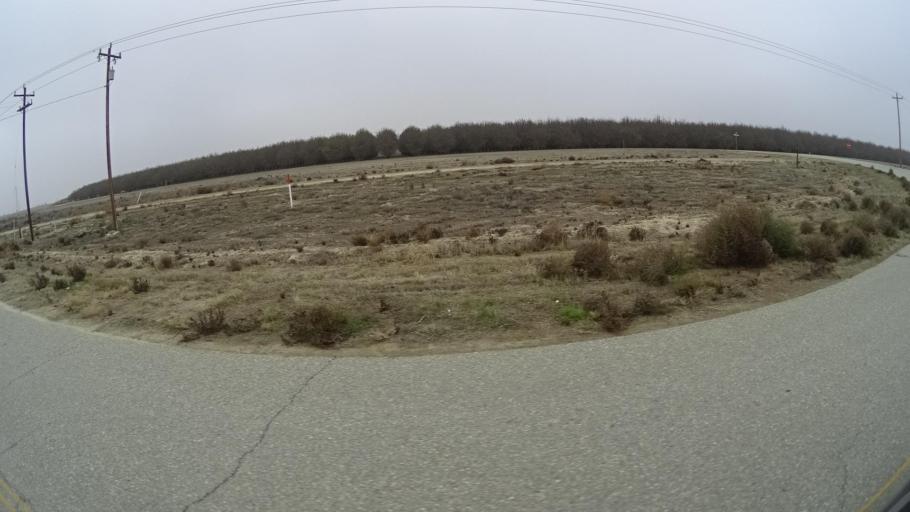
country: US
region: California
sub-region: Kern County
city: Lost Hills
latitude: 35.6009
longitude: -119.5723
